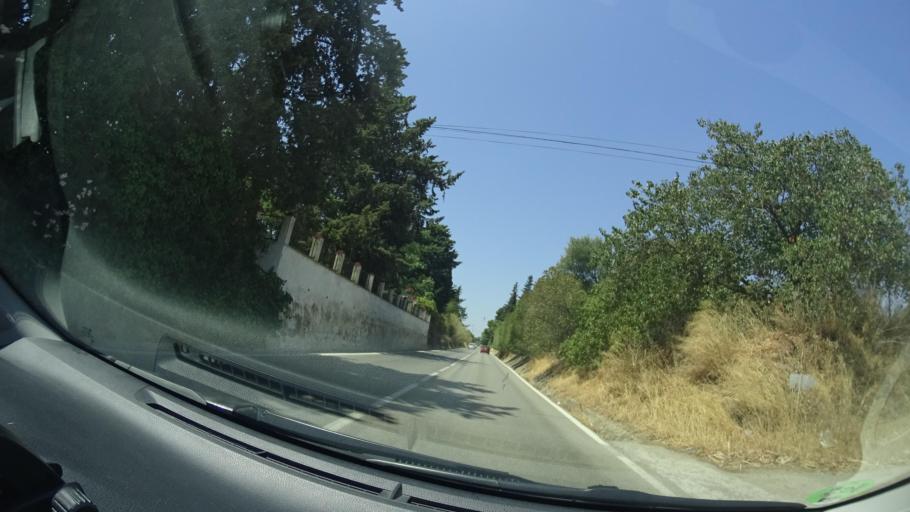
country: ES
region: Andalusia
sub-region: Provincia de Cadiz
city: Jerez de la Frontera
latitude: 36.6642
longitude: -6.1112
